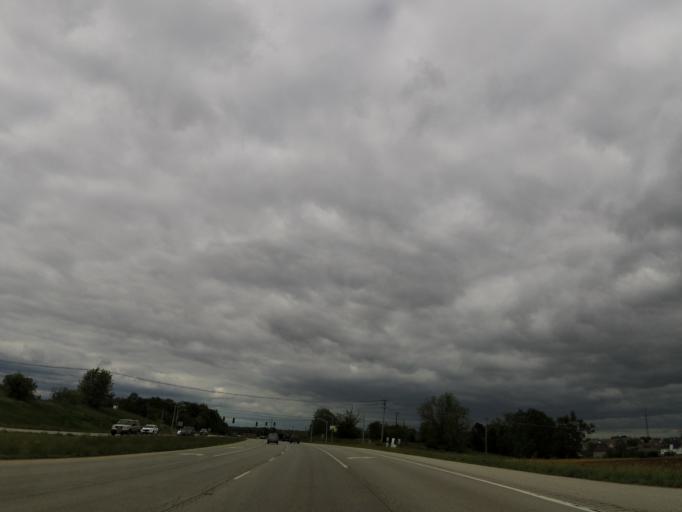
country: US
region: Kentucky
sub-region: Scott County
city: Georgetown
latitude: 38.1966
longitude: -84.5393
